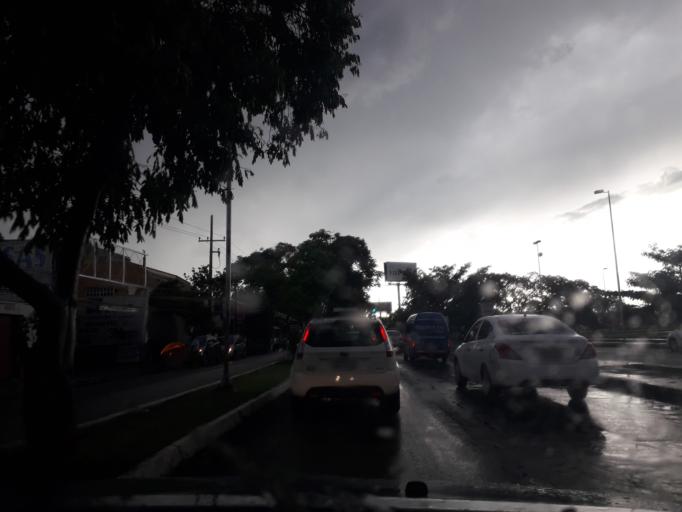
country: MX
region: Yucatan
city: Merida
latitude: 20.9781
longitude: -89.6449
